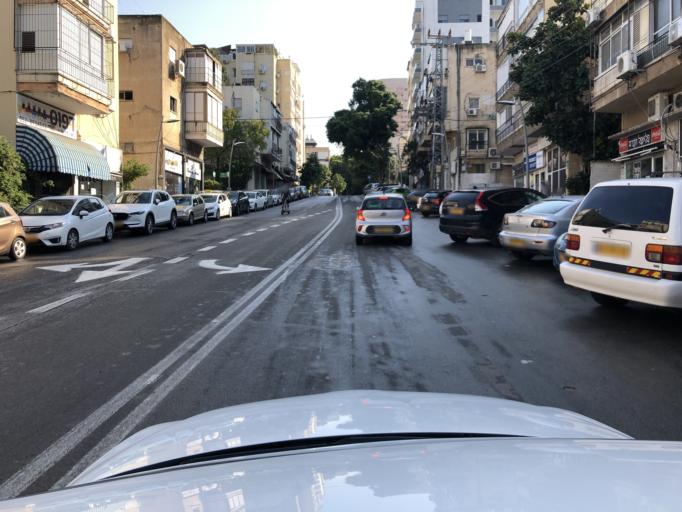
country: IL
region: Tel Aviv
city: Ramat Gan
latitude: 32.0932
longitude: 34.8174
